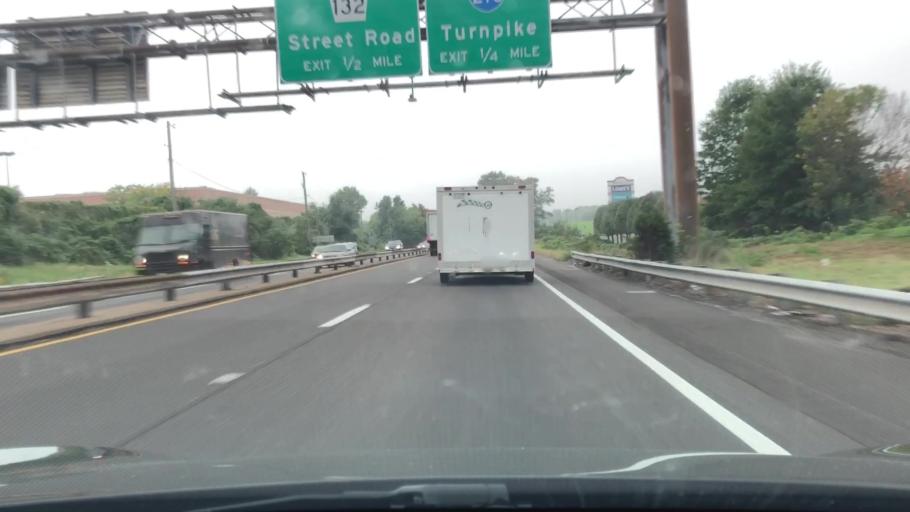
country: US
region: Pennsylvania
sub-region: Bucks County
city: Trevose
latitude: 40.1373
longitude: -74.9622
